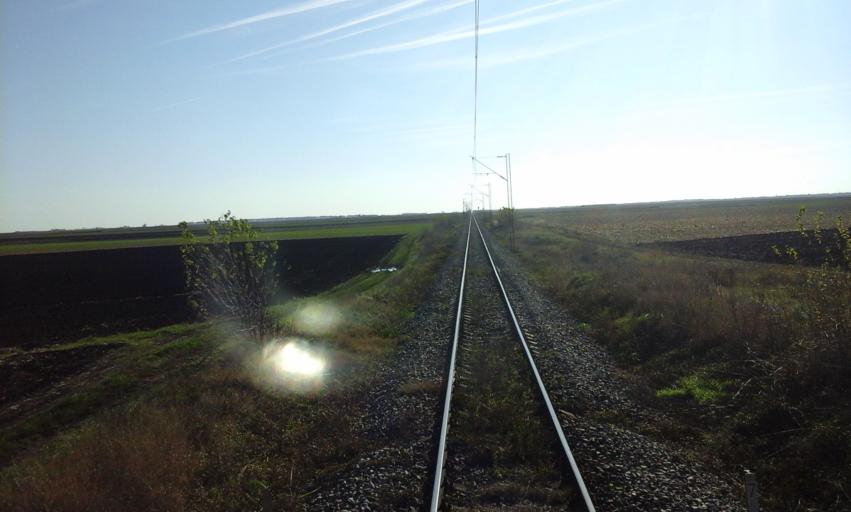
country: RS
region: Autonomna Pokrajina Vojvodina
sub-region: Severnobacki Okrug
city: Backa Topola
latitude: 45.9210
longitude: 19.6654
